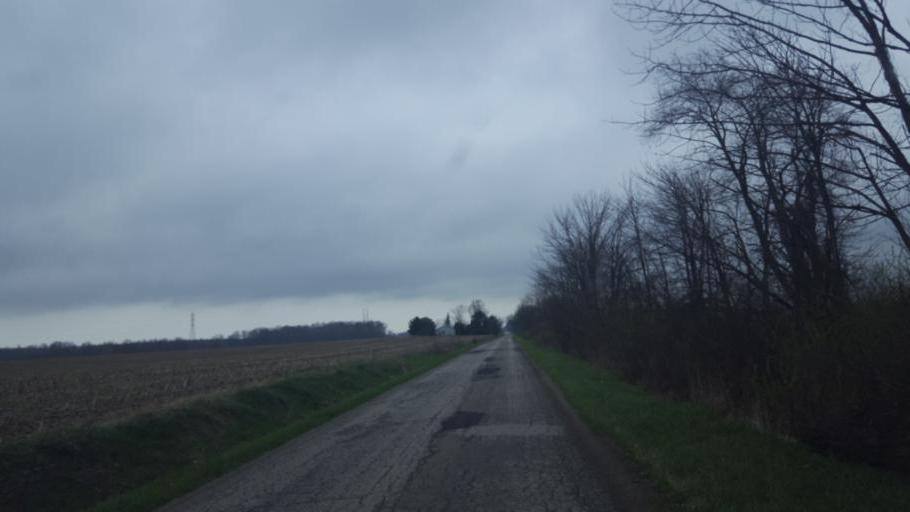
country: US
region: Ohio
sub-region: Crawford County
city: Galion
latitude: 40.7068
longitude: -82.7460
